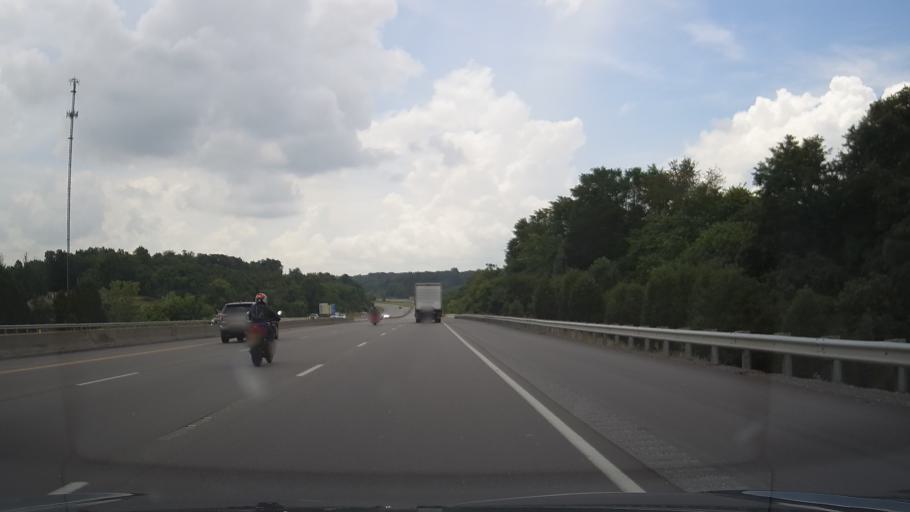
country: US
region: Kentucky
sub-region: Scott County
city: Georgetown
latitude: 38.3508
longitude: -84.5681
